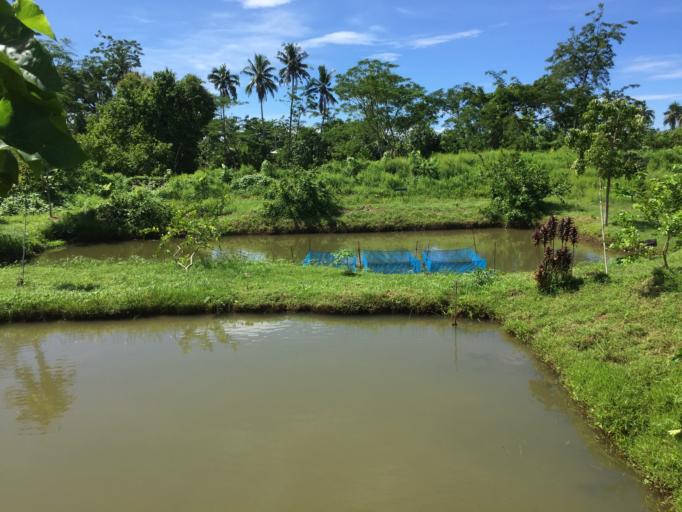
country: WS
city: Lotofaga
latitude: -13.9740
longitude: -171.8537
